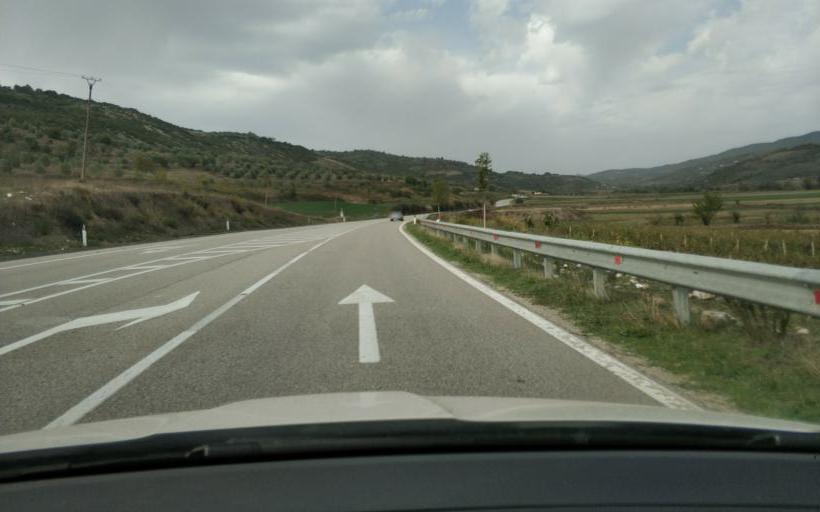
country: AL
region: Gjirokaster
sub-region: Rrethi i Tepelenes
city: Krahes
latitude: 40.4407
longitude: 19.8487
